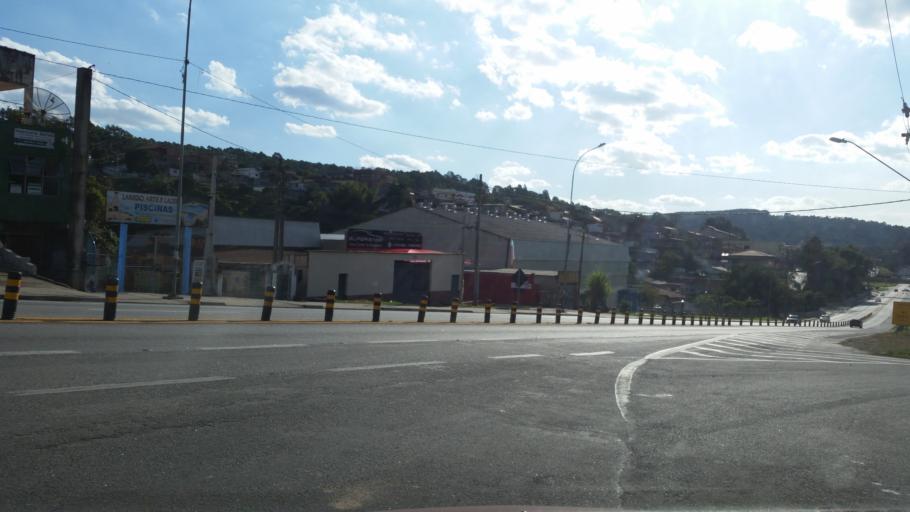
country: BR
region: Sao Paulo
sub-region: Mairinque
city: Mairinque
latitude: -23.5210
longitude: -47.2541
